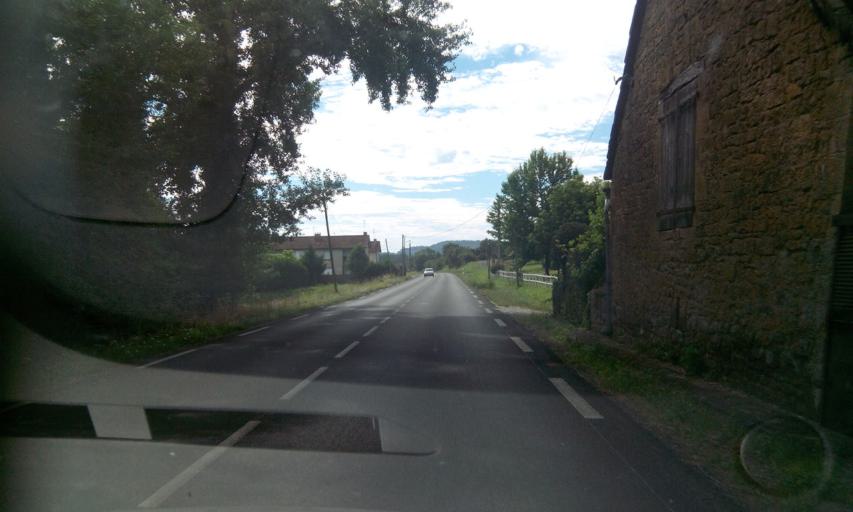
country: FR
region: Limousin
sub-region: Departement de la Correze
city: Meyssac
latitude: 45.0016
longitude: 1.6355
